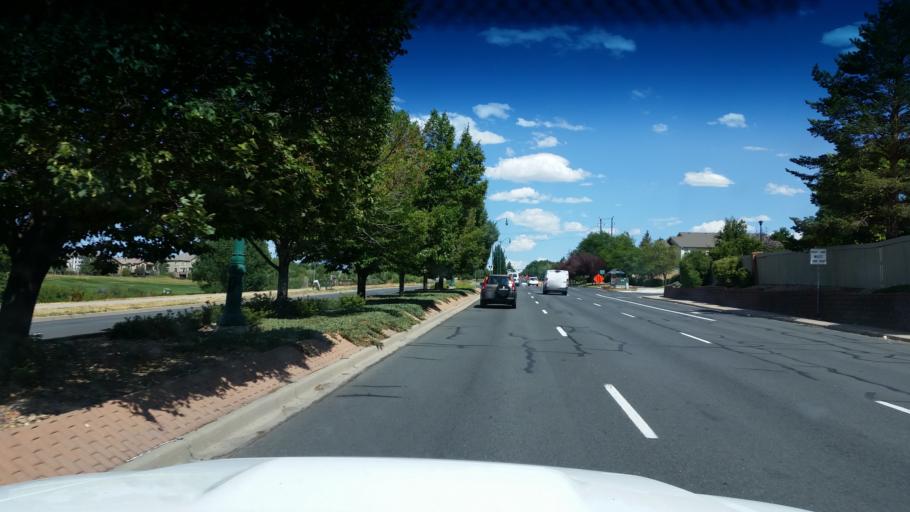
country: US
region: Colorado
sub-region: Adams County
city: Westminster
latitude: 39.8852
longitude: -105.0497
